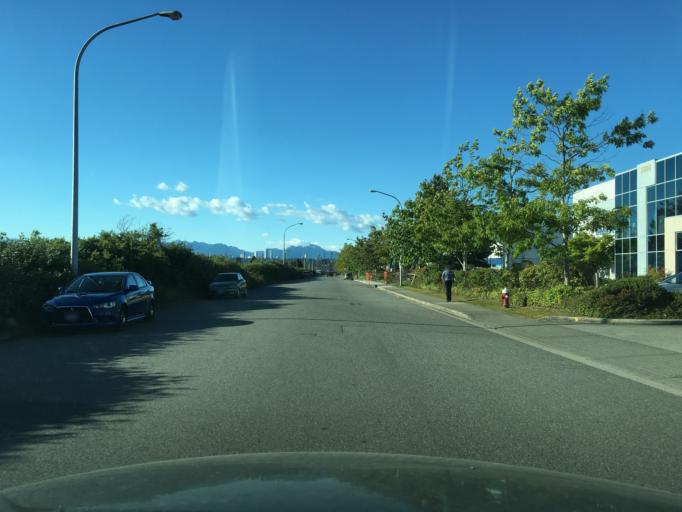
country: CA
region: British Columbia
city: Delta
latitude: 49.1656
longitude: -122.9940
